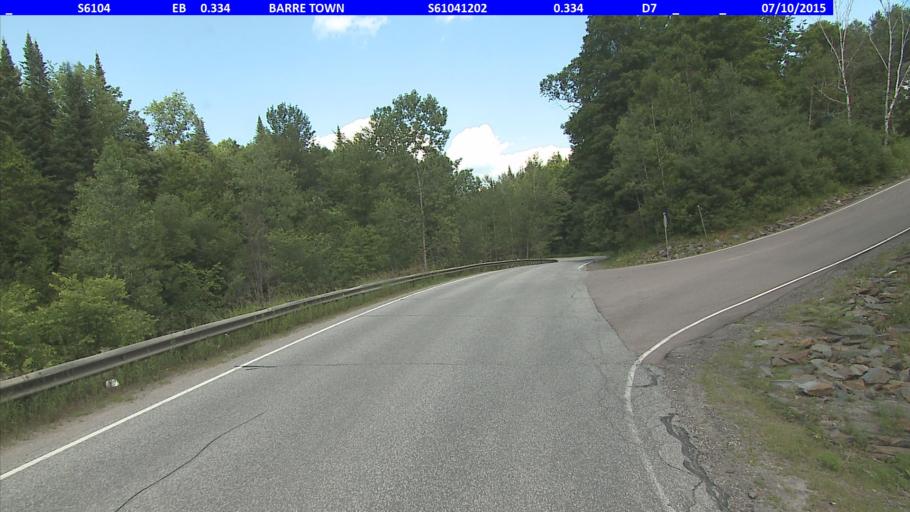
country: US
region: Vermont
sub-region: Washington County
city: Barre
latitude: 44.2207
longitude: -72.4852
